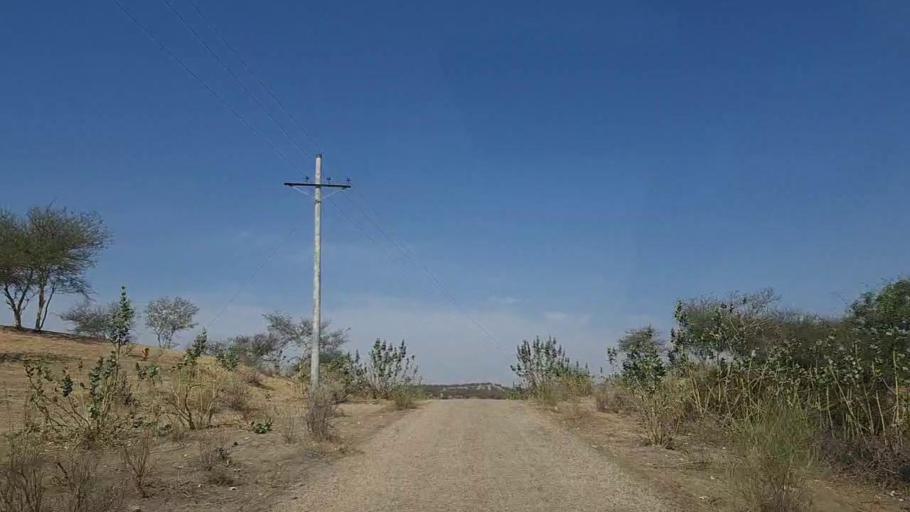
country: PK
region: Sindh
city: Mithi
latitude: 24.8425
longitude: 69.6675
